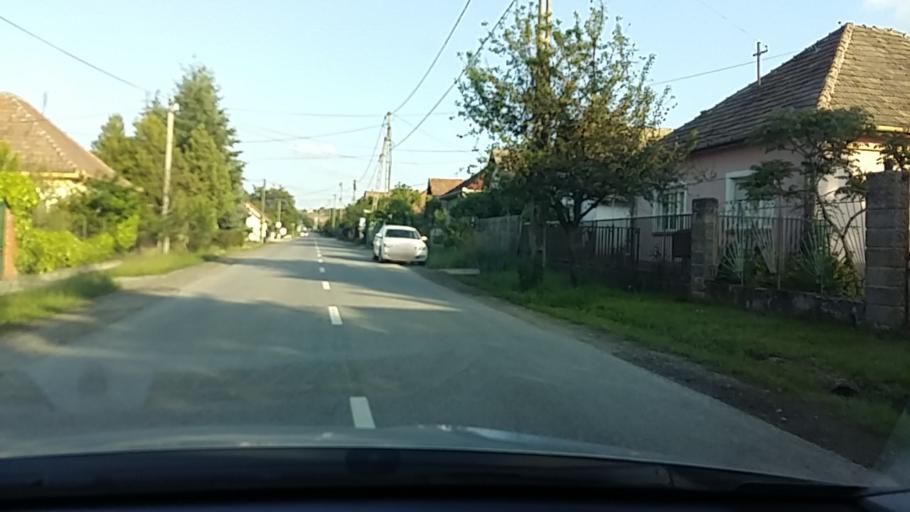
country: HU
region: Pest
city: Szod
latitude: 47.7458
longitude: 19.2109
